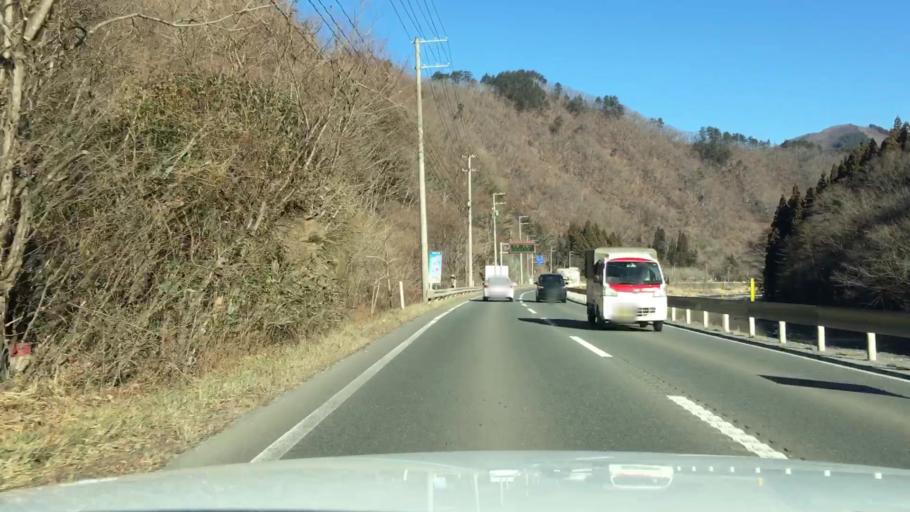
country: JP
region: Iwate
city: Miyako
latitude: 39.6113
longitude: 141.7881
